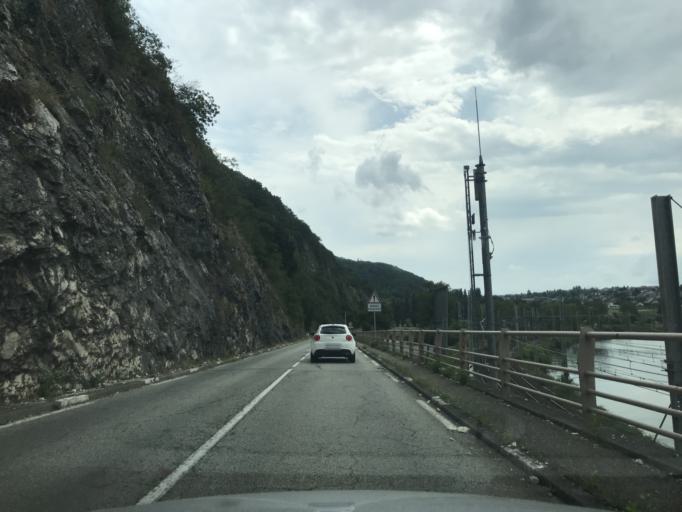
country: FR
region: Rhone-Alpes
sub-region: Departement de la Savoie
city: Brison-Saint-Innocent
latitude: 45.7392
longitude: 5.8920
